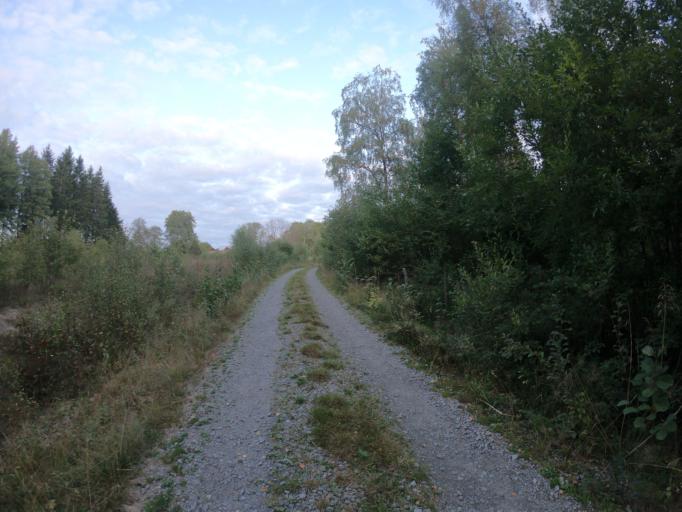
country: SE
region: Joenkoeping
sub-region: Vetlanda Kommun
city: Landsbro
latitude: 57.3219
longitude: 14.8632
